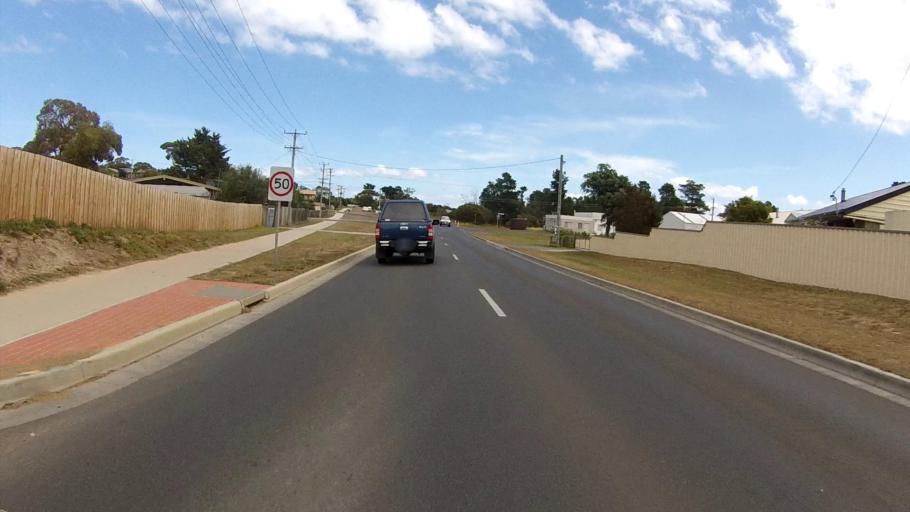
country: AU
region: Tasmania
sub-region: Sorell
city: Sorell
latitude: -42.8585
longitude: 147.6154
